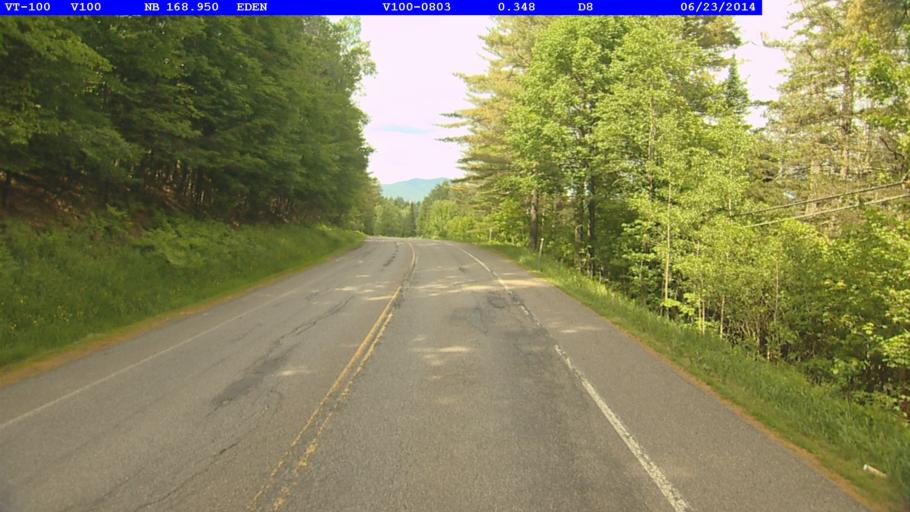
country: US
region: Vermont
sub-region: Lamoille County
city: Hyde Park
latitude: 44.6882
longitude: -72.5876
